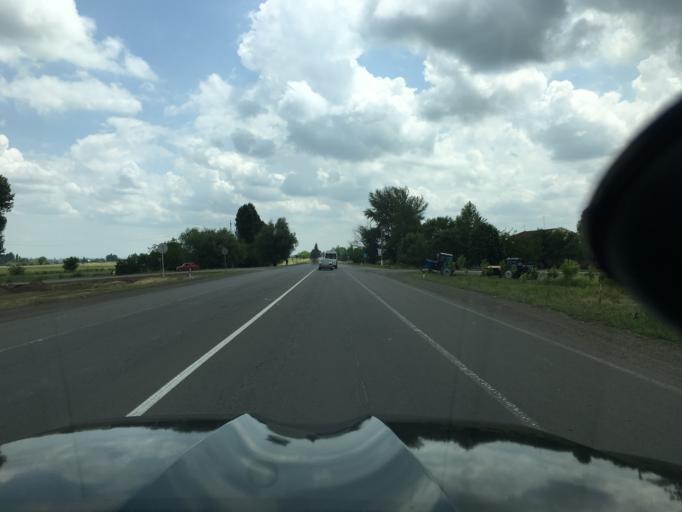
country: AZ
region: Tovuz
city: Tovuz
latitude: 40.9568
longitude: 45.7328
